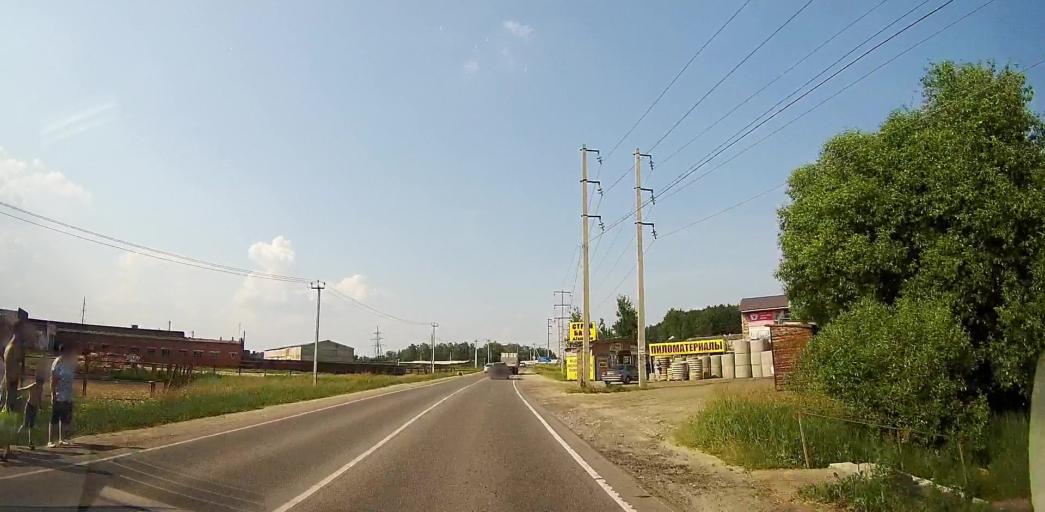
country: RU
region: Moskovskaya
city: Barybino
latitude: 55.2769
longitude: 37.9161
